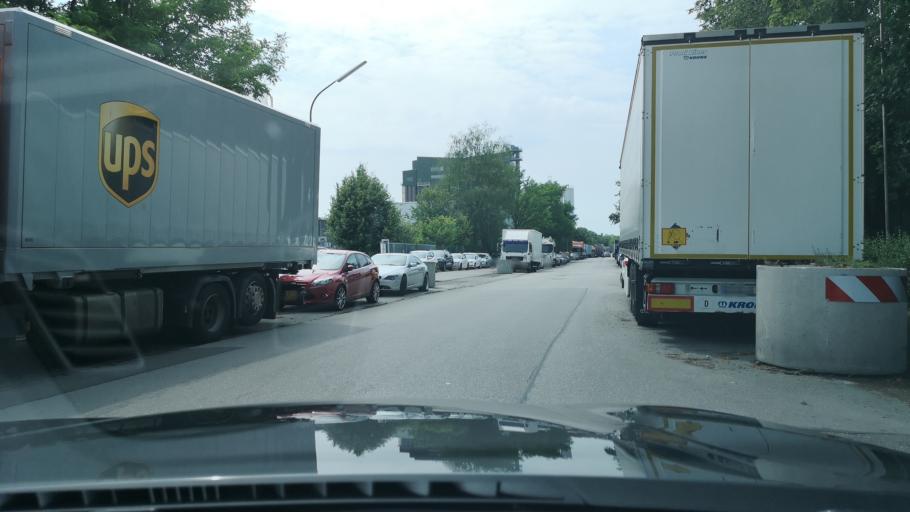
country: DE
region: Bavaria
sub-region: Upper Bavaria
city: Garching bei Munchen
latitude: 48.2548
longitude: 11.6109
